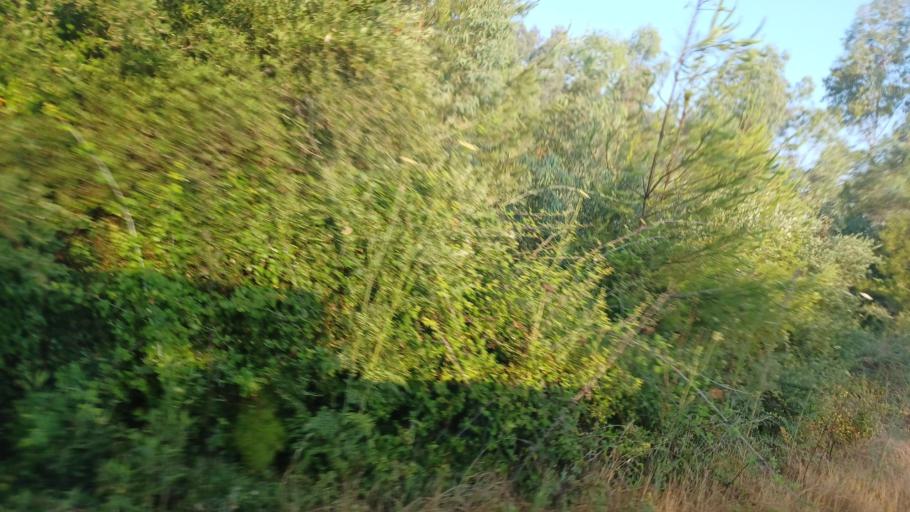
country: CY
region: Larnaka
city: Mosfiloti
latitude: 34.9761
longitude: 33.4198
